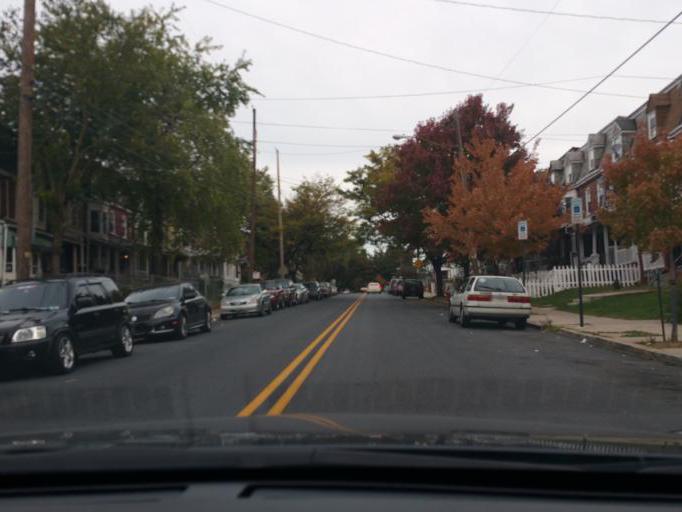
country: US
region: Pennsylvania
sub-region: Lancaster County
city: Lancaster
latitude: 40.0339
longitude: -76.2938
